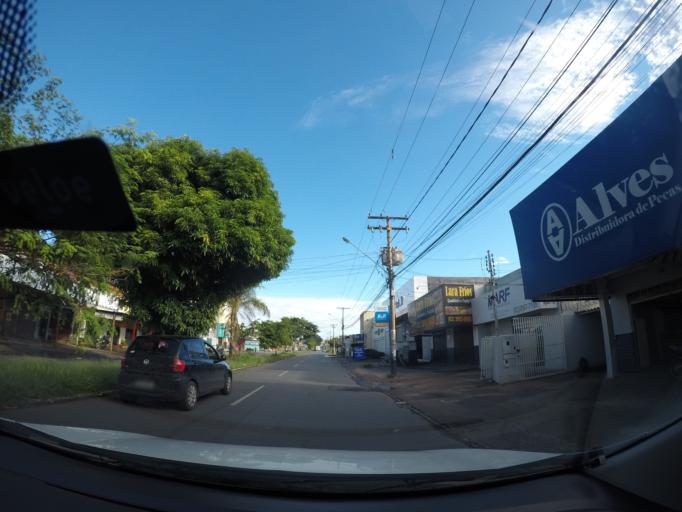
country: BR
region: Goias
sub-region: Goiania
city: Goiania
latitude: -16.7517
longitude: -49.2797
